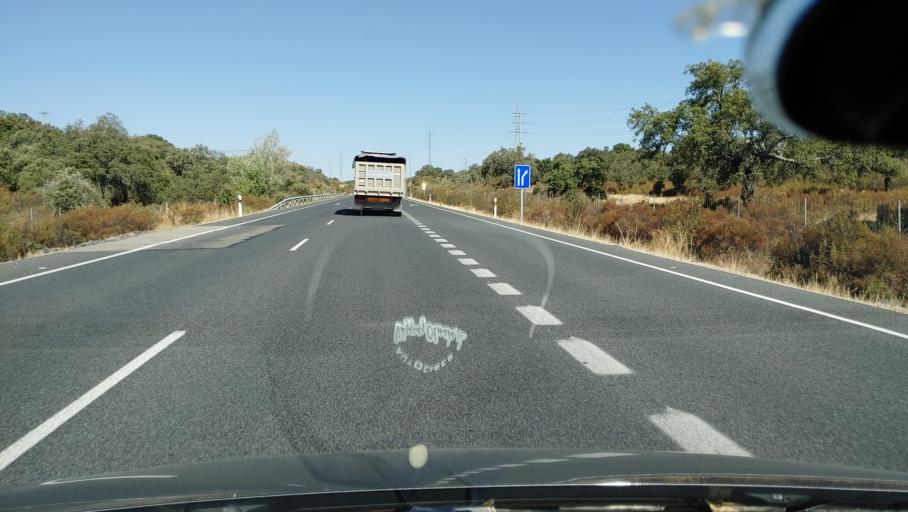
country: ES
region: Andalusia
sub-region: Province of Cordoba
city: Villaharta
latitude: 38.0855
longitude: -4.8577
